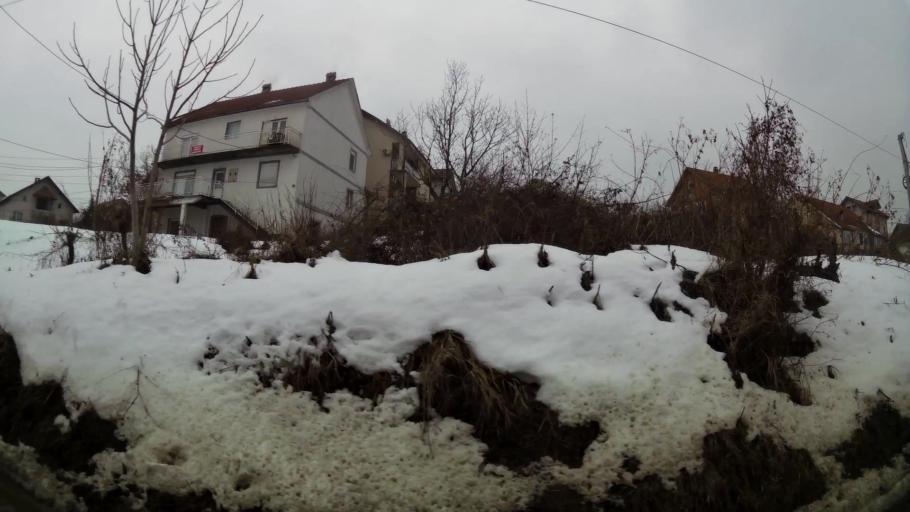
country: RS
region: Central Serbia
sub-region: Belgrade
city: Zvezdara
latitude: 44.7666
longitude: 20.5095
